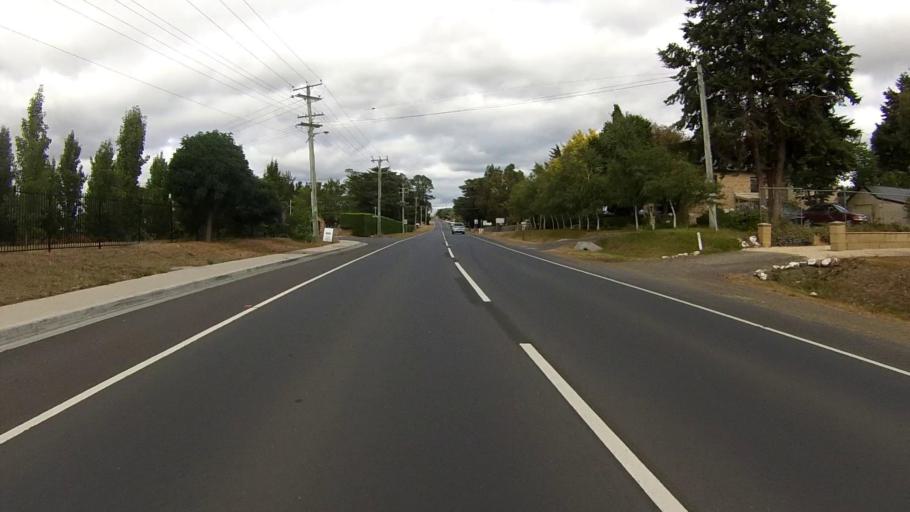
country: AU
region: Tasmania
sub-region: Brighton
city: Bridgewater
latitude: -42.6861
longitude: 147.2652
